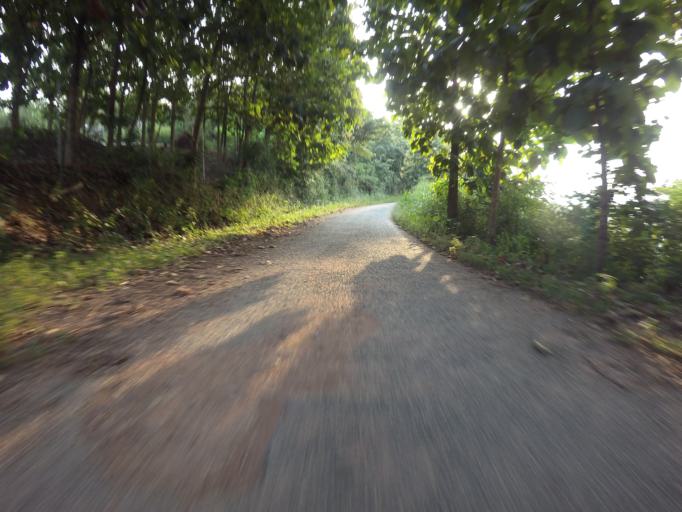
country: TG
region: Plateaux
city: Kpalime
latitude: 6.8885
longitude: 0.4497
